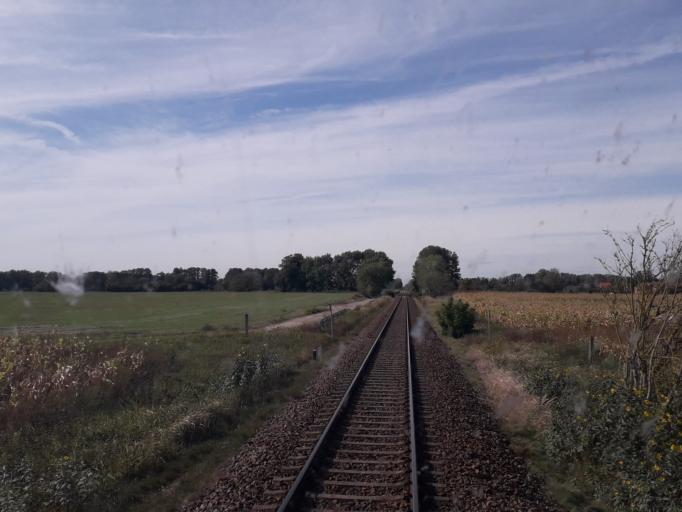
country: DE
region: Brandenburg
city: Kremmen
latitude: 52.8074
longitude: 13.0141
